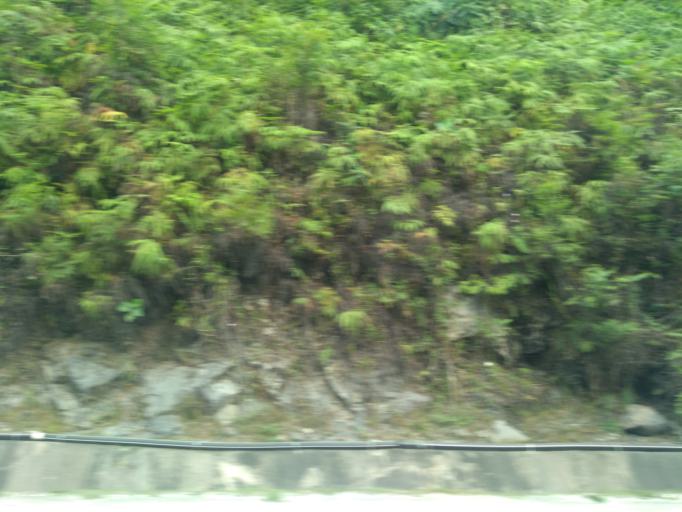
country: MY
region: Perak
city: Ipoh
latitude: 4.5451
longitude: 101.1595
